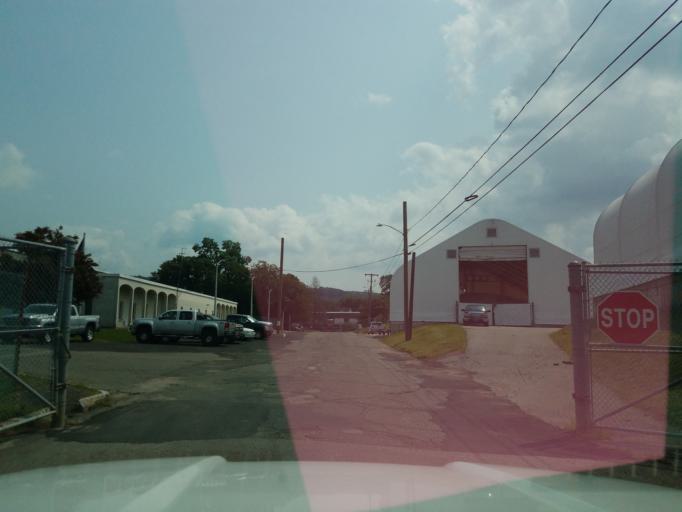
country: US
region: Connecticut
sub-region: Litchfield County
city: Torrington
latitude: 41.7942
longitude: -73.1162
